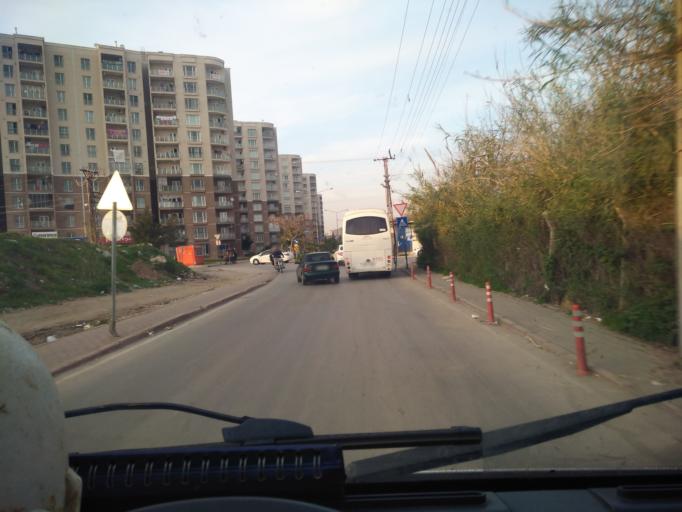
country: TR
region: Adana
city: Seyhan
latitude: 37.0066
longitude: 35.2803
